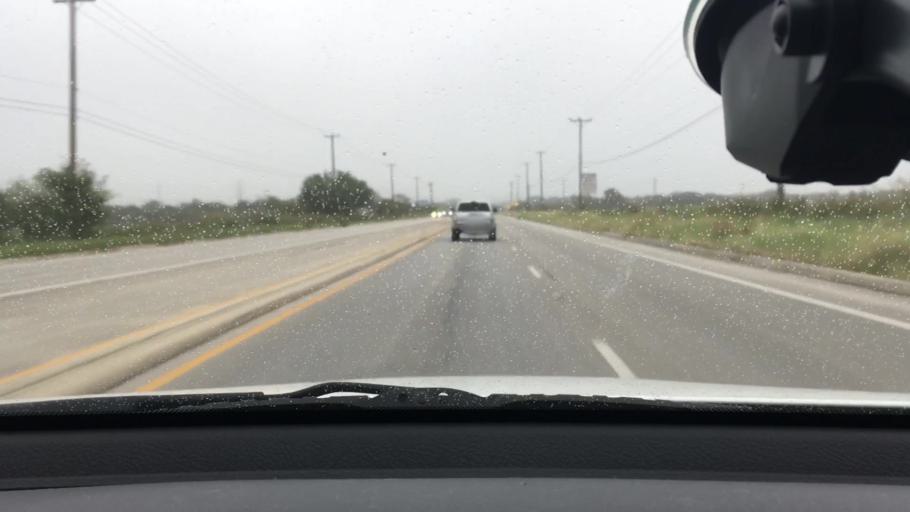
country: US
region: Texas
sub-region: Bexar County
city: Selma
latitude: 29.6022
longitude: -98.3317
